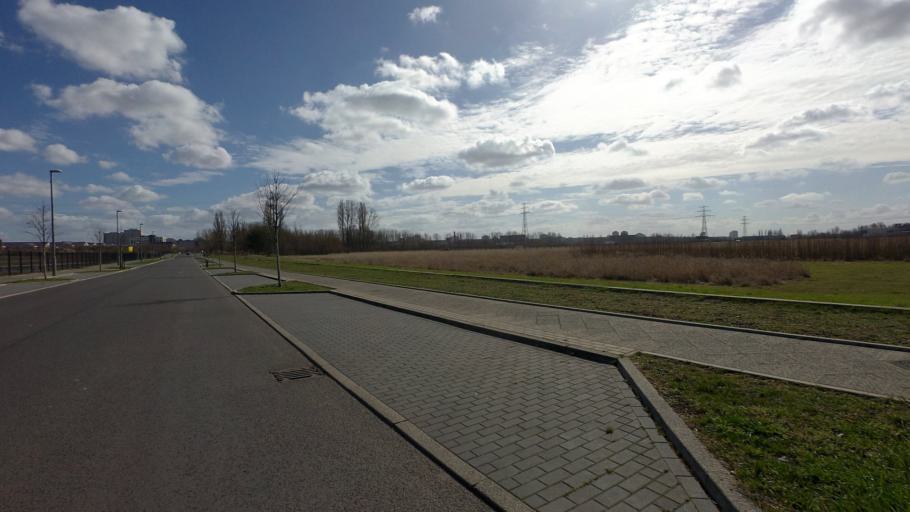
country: DE
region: Berlin
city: Falkenberg
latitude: 52.5609
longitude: 13.5371
